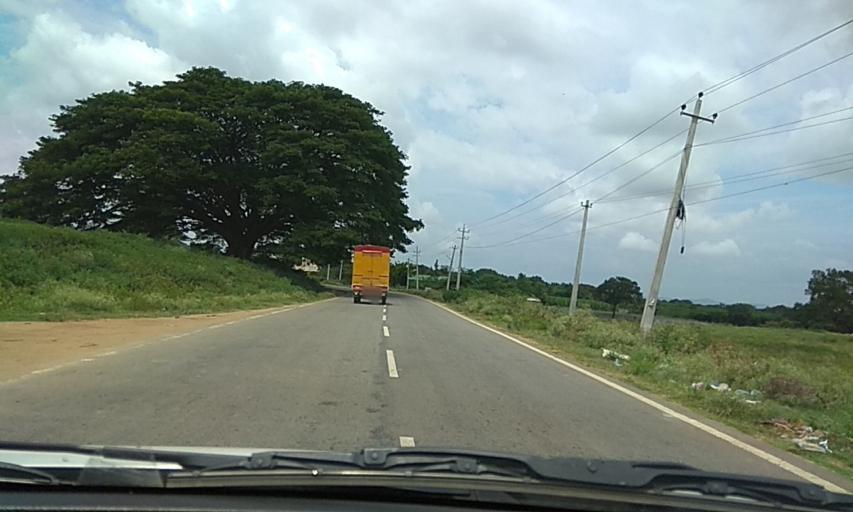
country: IN
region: Karnataka
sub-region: Chamrajnagar
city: Gundlupet
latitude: 11.8147
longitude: 76.7839
